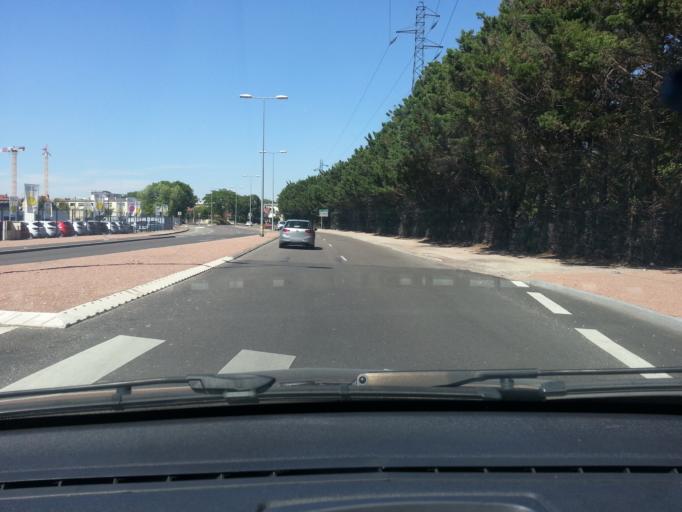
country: FR
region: Bourgogne
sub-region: Departement de la Cote-d'Or
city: Dijon
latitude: 47.3018
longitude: 5.0250
